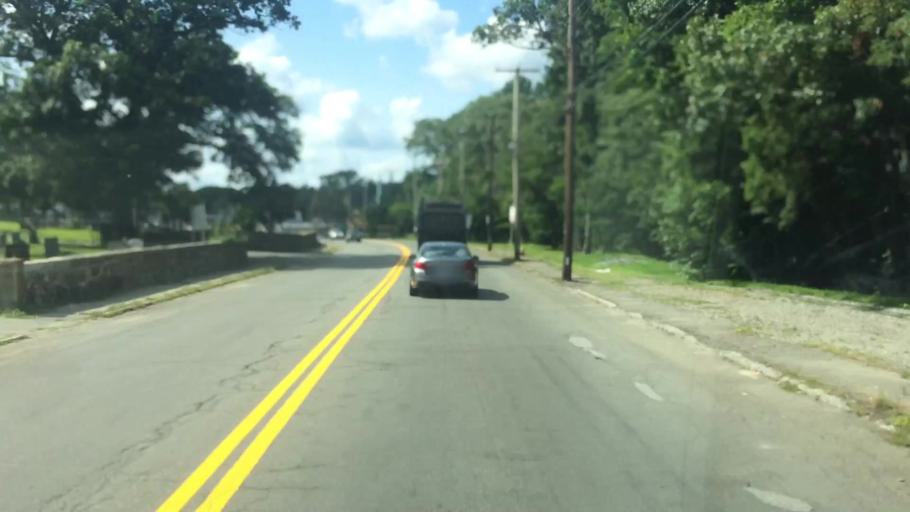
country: US
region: Massachusetts
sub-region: Essex County
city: South Peabody
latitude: 42.4903
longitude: -70.9697
